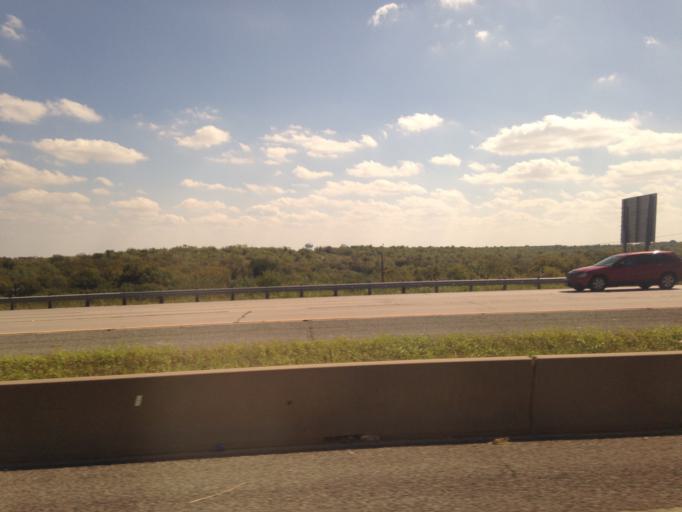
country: US
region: Texas
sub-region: Tarrant County
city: Sansom Park
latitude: 32.8221
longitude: -97.3951
